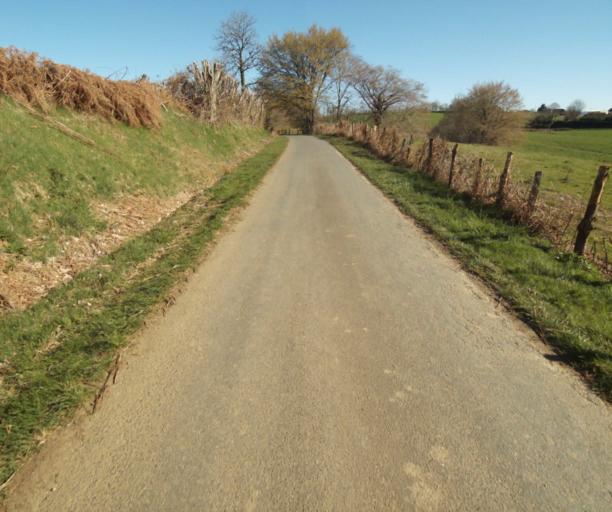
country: FR
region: Limousin
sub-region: Departement de la Correze
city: Chamboulive
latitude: 45.4022
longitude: 1.7096
